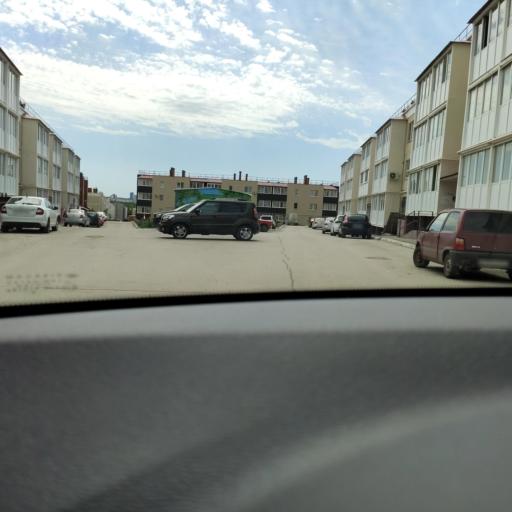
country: RU
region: Samara
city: Samara
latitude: 53.2906
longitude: 50.2221
